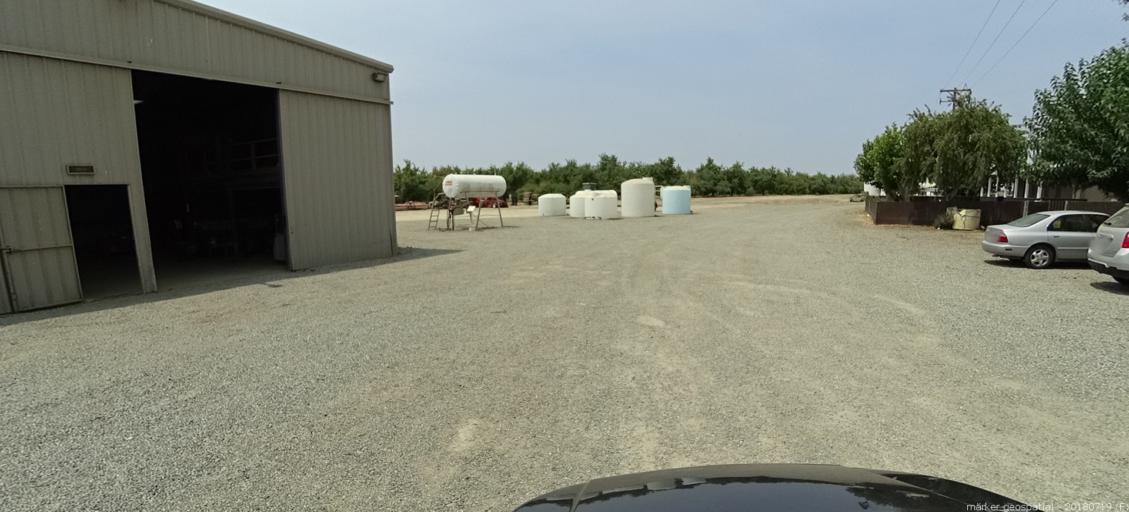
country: US
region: California
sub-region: Madera County
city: Fairmead
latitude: 37.0908
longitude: -120.1295
